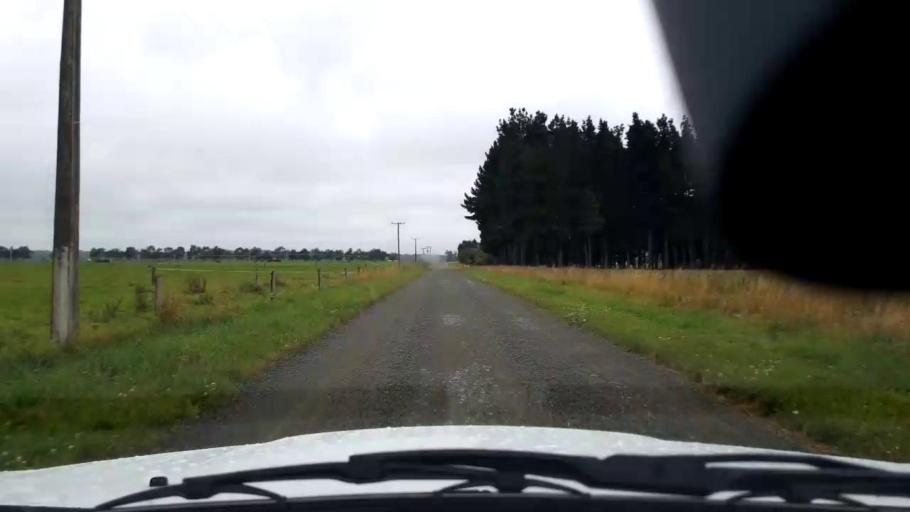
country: NZ
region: Canterbury
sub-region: Timaru District
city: Pleasant Point
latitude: -44.2409
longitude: 171.2016
